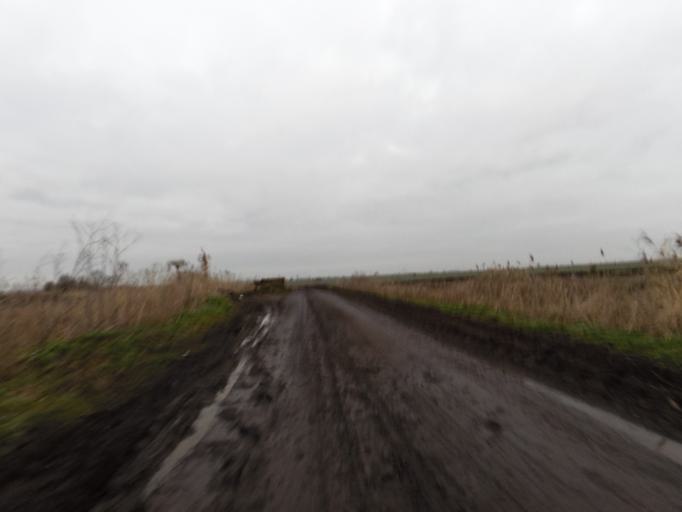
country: GB
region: England
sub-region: Cambridgeshire
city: Bottisham
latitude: 52.2810
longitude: 0.2677
